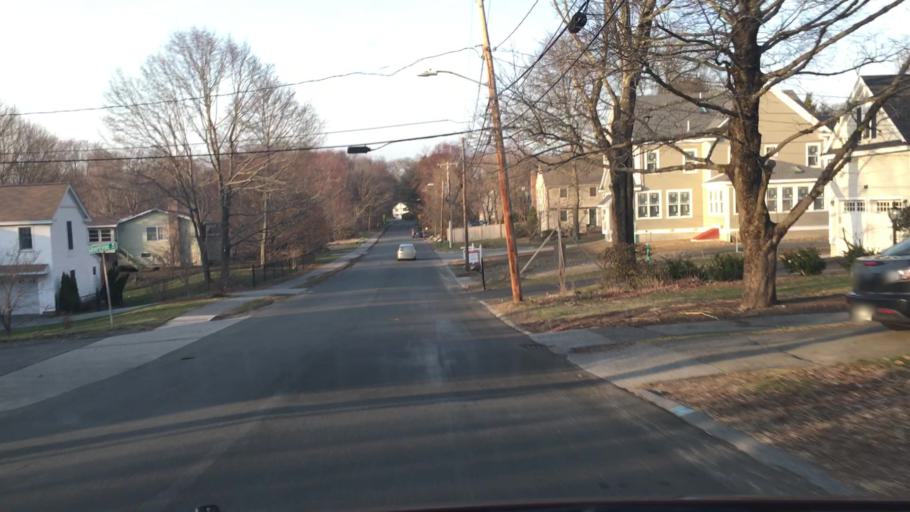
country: US
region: Massachusetts
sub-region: Middlesex County
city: Lexington
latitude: 42.4352
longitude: -71.2308
